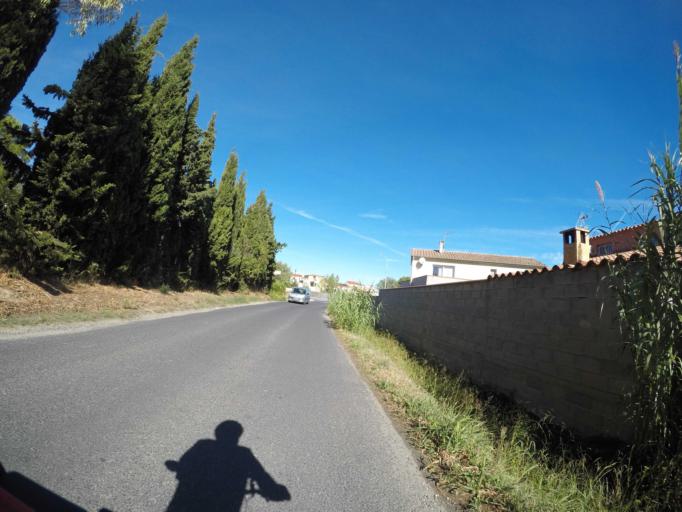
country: FR
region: Languedoc-Roussillon
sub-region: Departement des Pyrenees-Orientales
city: Ponteilla
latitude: 42.6282
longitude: 2.8122
